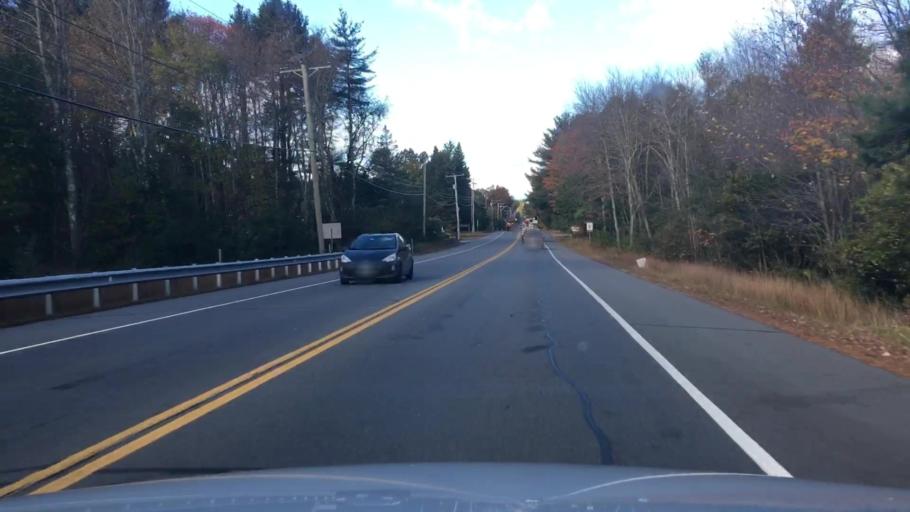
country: US
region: New Hampshire
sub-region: Strafford County
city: Lee
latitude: 43.1500
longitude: -71.0143
